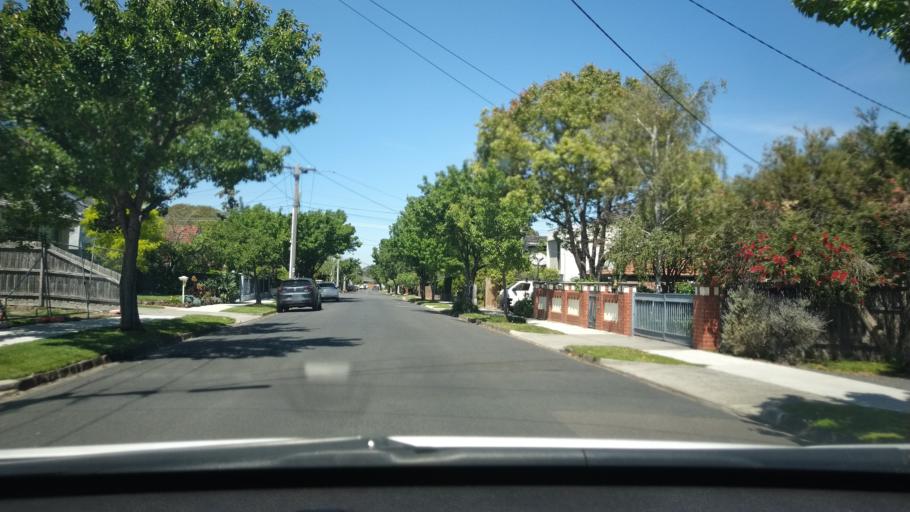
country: AU
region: Victoria
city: Ormond
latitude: -37.8896
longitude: 145.0353
